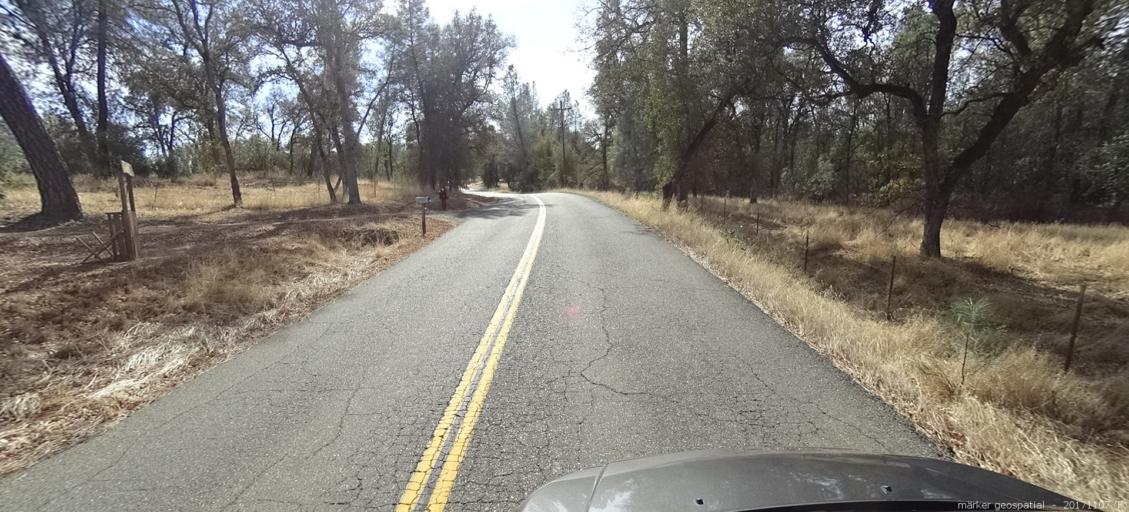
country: US
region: California
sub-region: Shasta County
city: Shasta
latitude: 40.4045
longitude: -122.5195
